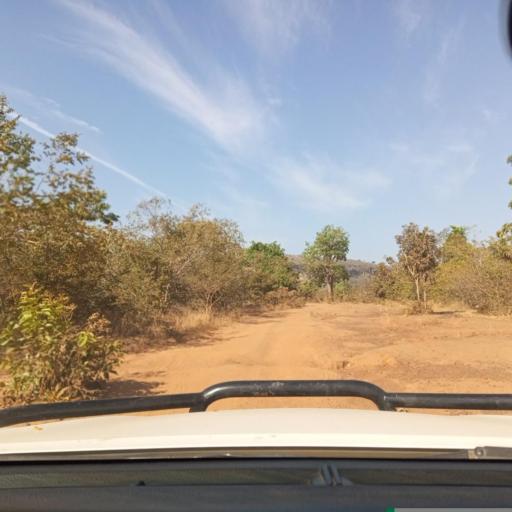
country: ML
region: Bamako
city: Bamako
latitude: 12.5556
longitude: -8.1430
